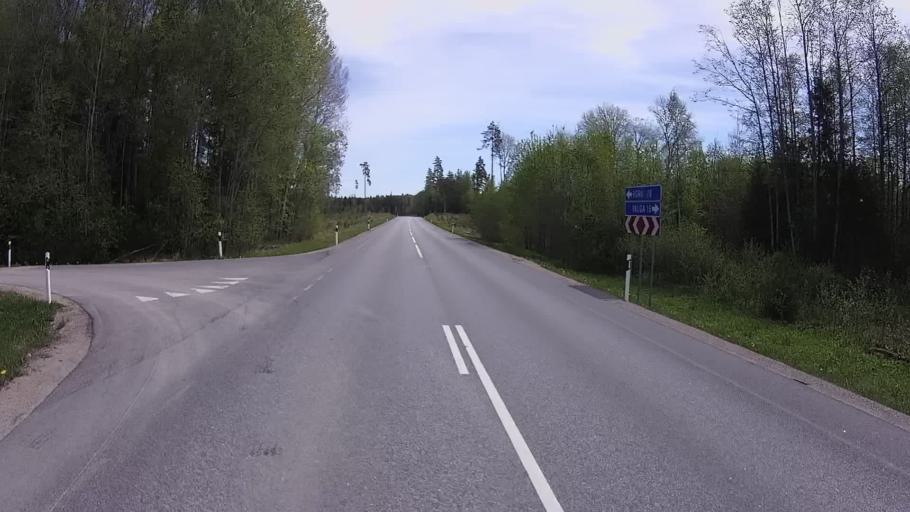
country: EE
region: Valgamaa
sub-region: Valga linn
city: Valga
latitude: 57.7084
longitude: 26.2337
